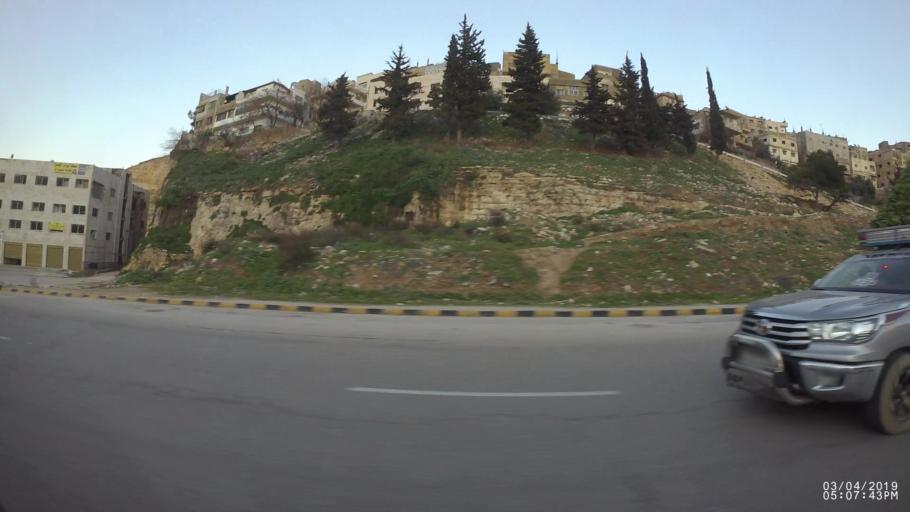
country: JO
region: Amman
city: Al Bunayyat ash Shamaliyah
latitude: 31.9240
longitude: 35.9112
